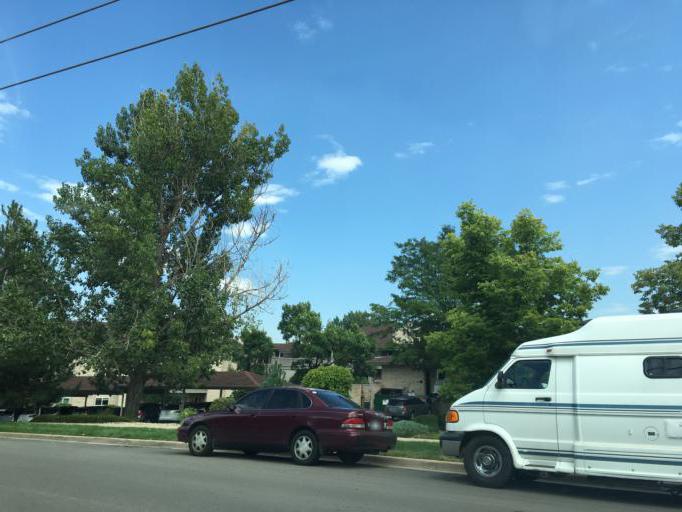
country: US
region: Colorado
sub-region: Jefferson County
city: Applewood
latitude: 39.7451
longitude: -105.1190
